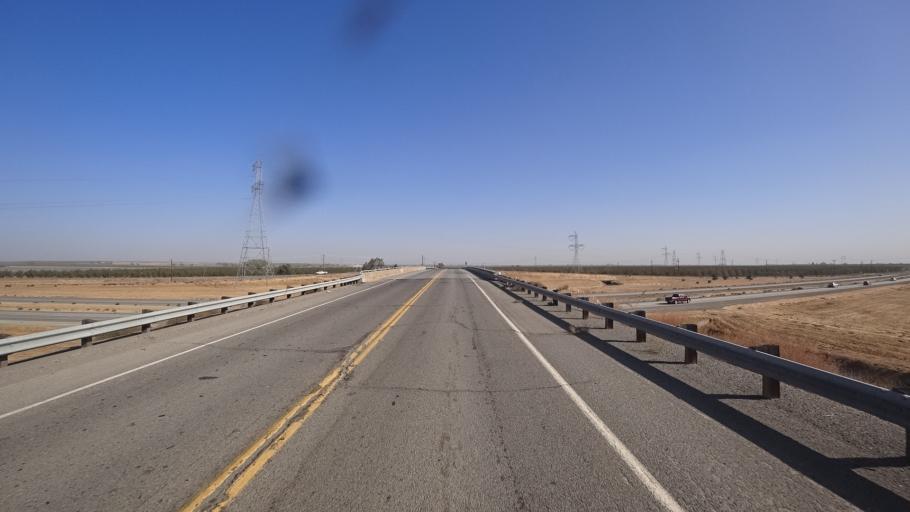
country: US
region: California
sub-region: Yolo County
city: Cottonwood
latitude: 38.7201
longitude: -121.9599
